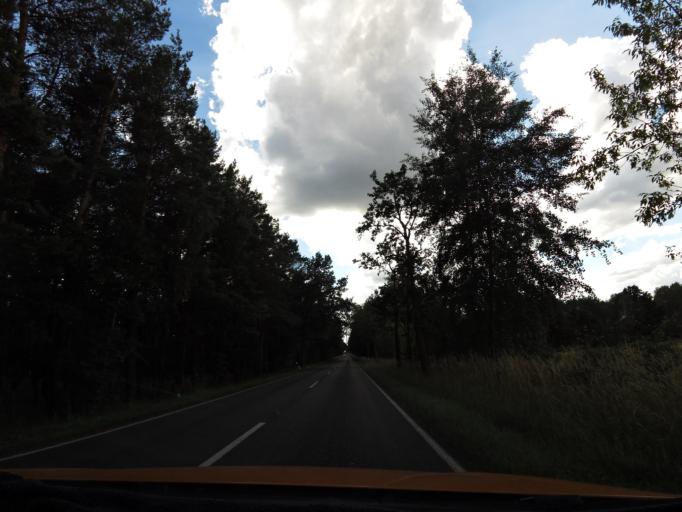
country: DE
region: Brandenburg
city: Erkner
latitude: 52.3110
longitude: 13.7442
